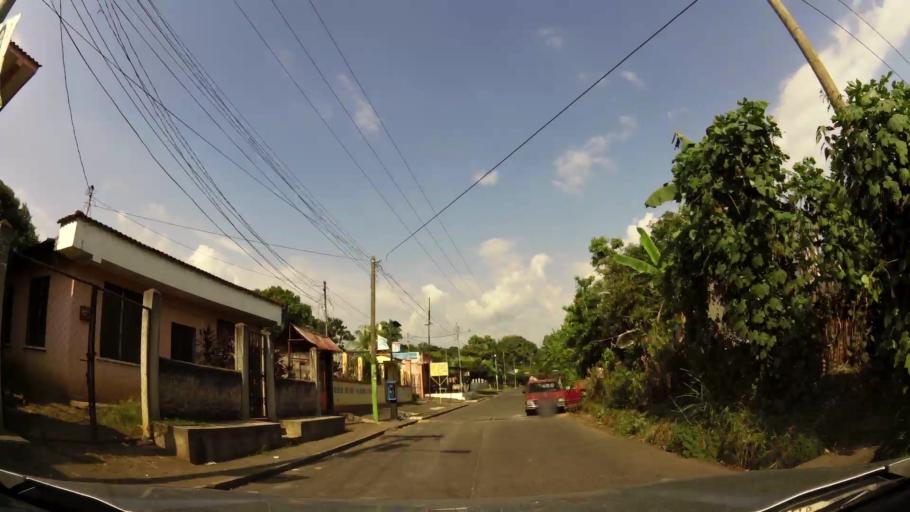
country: GT
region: Retalhuleu
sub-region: Municipio de Retalhuleu
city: Retalhuleu
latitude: 14.5361
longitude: -91.6885
